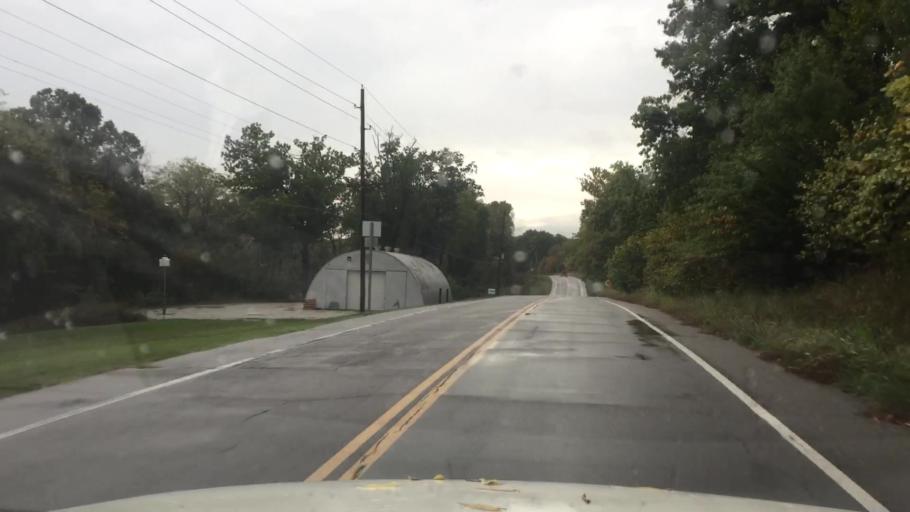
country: US
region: Missouri
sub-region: Boone County
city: Columbia
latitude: 38.8814
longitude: -92.4218
